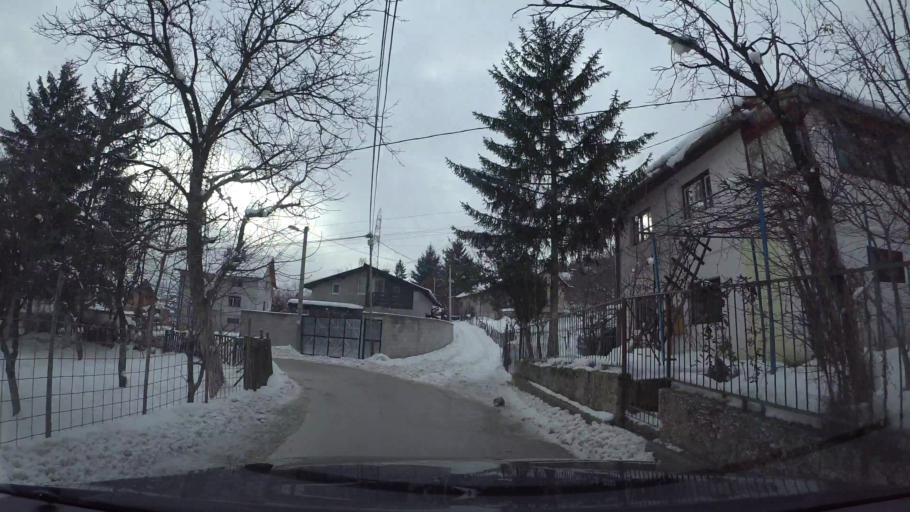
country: BA
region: Federation of Bosnia and Herzegovina
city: Kobilja Glava
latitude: 43.8704
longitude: 18.3947
